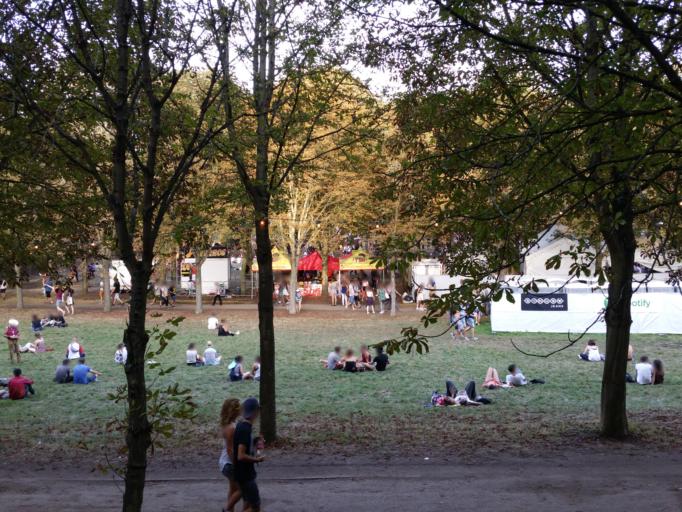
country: FR
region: Ile-de-France
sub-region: Departement des Hauts-de-Seine
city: Sevres
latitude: 48.8337
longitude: 2.2201
